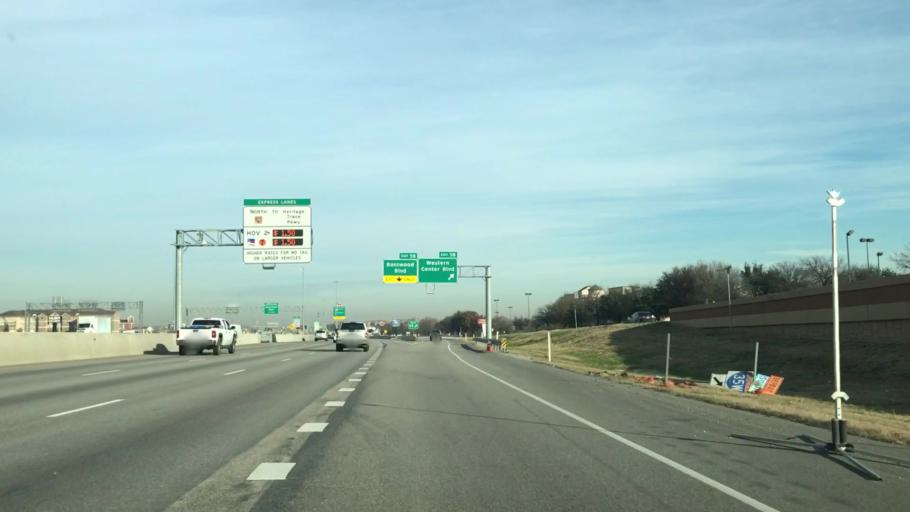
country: US
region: Texas
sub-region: Tarrant County
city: Blue Mound
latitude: 32.8518
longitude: -97.3125
